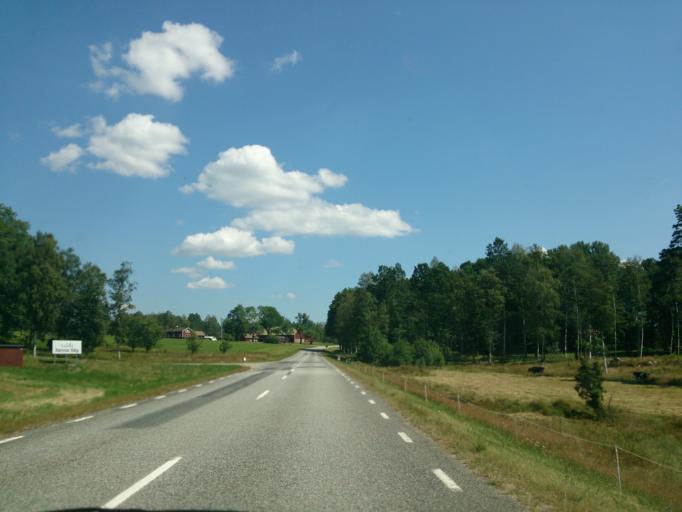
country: SE
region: Joenkoeping
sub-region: Varnamo Kommun
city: Forsheda
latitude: 57.0631
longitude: 13.9138
